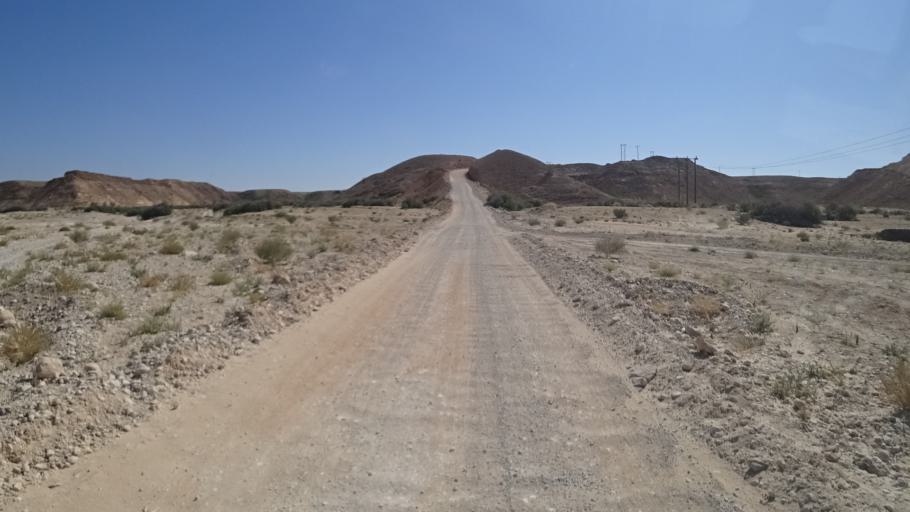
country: YE
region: Al Mahrah
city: Hawf
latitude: 17.3738
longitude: 53.1930
